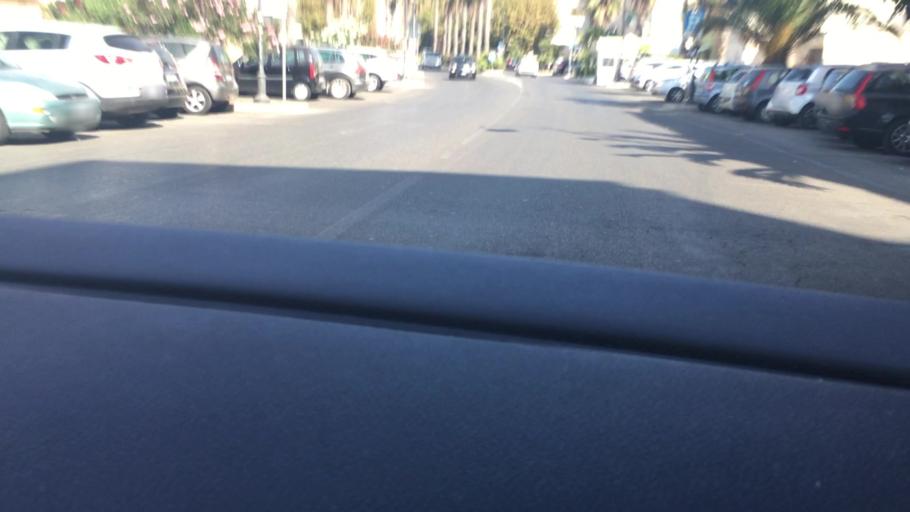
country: IT
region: Latium
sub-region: Citta metropolitana di Roma Capitale
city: Anzio
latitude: 41.4458
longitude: 12.6242
